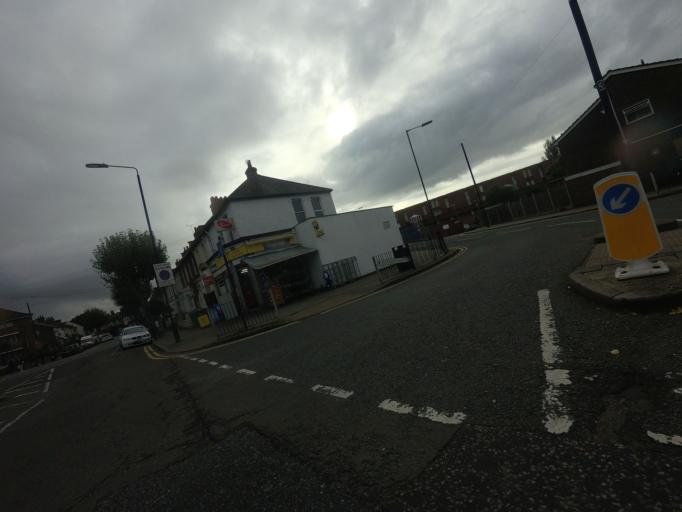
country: GB
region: England
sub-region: Greater London
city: East Ham
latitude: 51.5242
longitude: 0.0396
